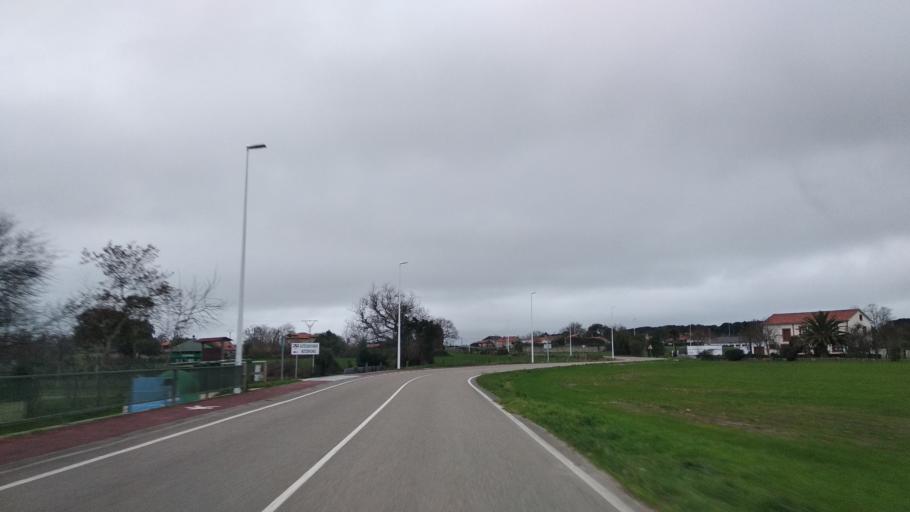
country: ES
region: Cantabria
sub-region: Provincia de Cantabria
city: Santander
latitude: 43.4472
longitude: -3.7272
